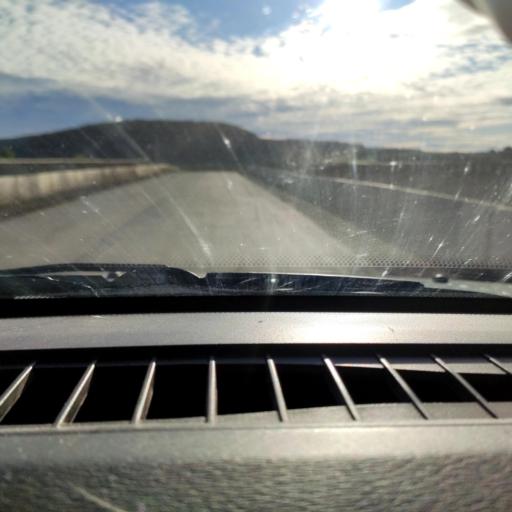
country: RU
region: Perm
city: Uinskoye
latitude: 57.0750
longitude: 56.5973
